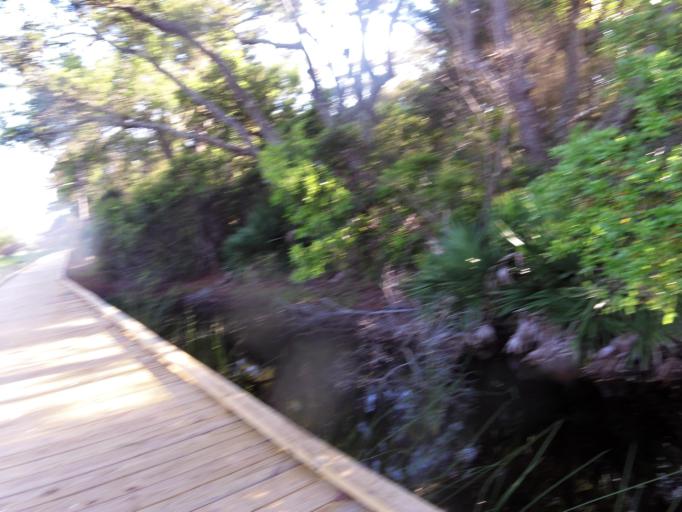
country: US
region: Florida
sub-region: Saint Johns County
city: Villano Beach
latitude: 30.0231
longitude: -81.3380
